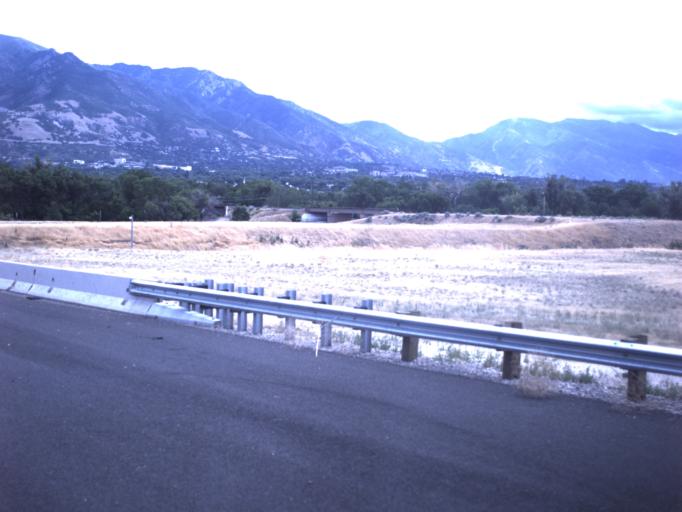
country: US
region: Utah
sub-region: Weber County
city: South Ogden
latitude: 41.2052
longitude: -111.9956
